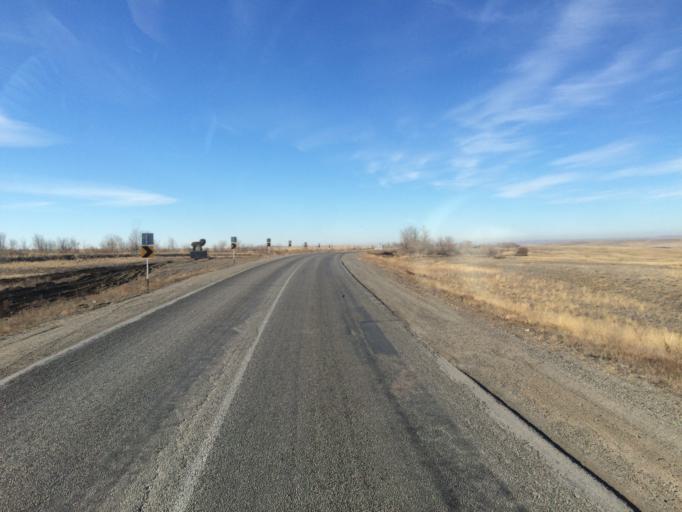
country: KZ
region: Aqtoebe
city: Aqtobe
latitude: 50.2819
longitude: 57.7513
